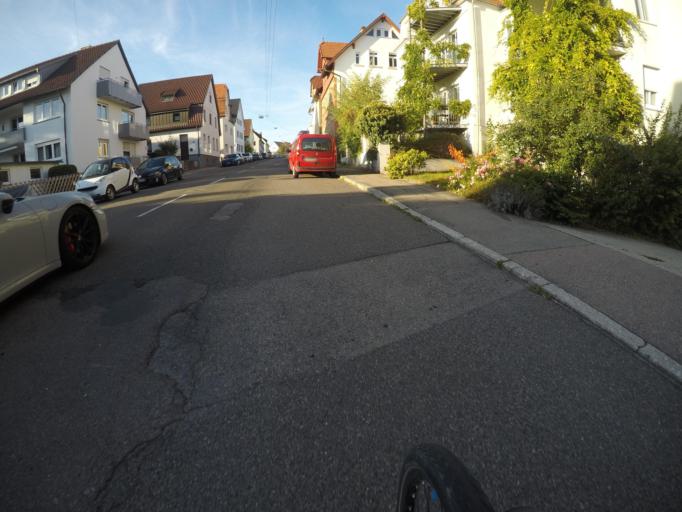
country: DE
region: Baden-Wuerttemberg
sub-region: Regierungsbezirk Stuttgart
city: Stuttgart
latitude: 48.7427
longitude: 9.1692
